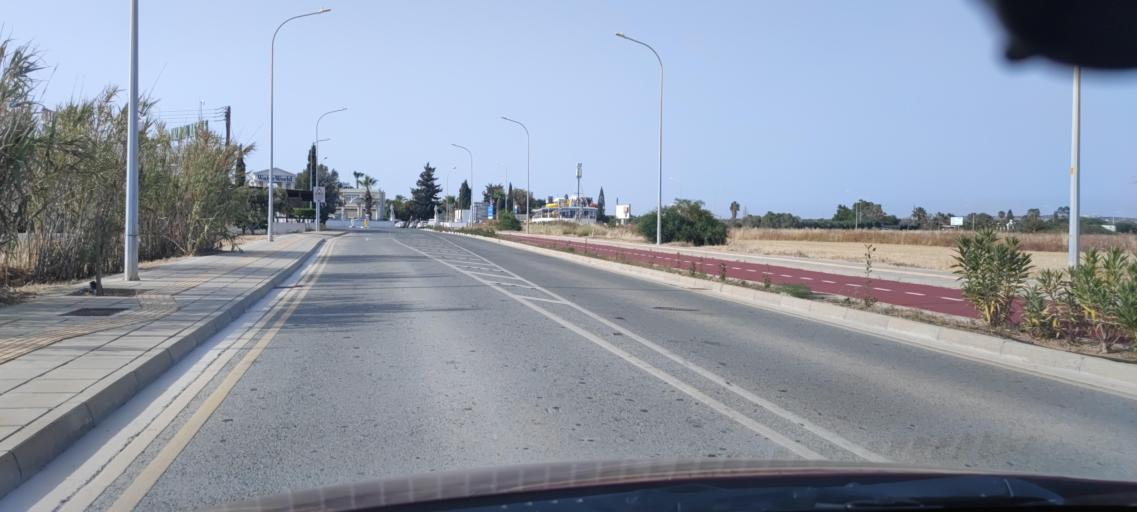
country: CY
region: Ammochostos
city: Liopetri
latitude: 34.9832
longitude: 33.9438
